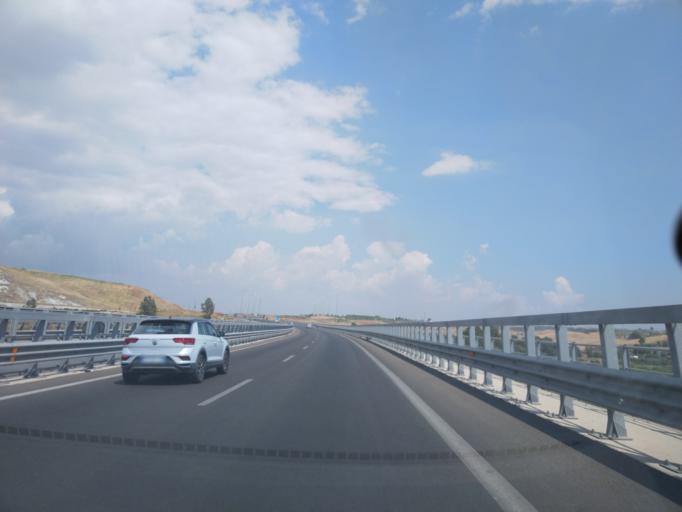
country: IT
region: Sicily
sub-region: Agrigento
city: Favara
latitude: 37.3445
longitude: 13.6470
